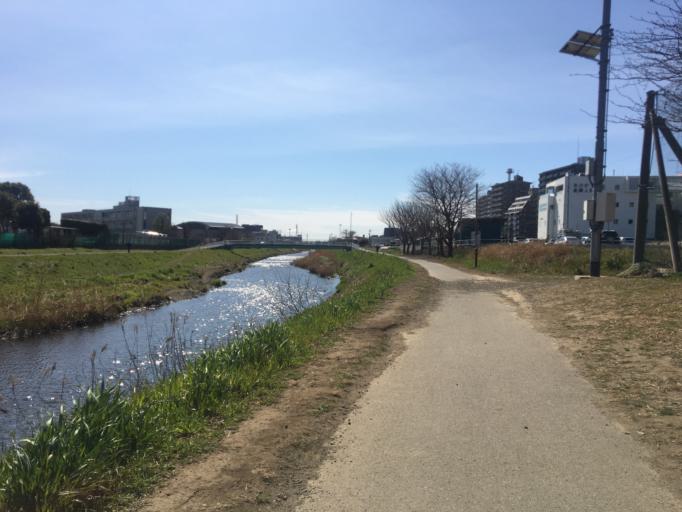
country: JP
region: Saitama
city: Asaka
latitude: 35.8075
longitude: 139.5848
